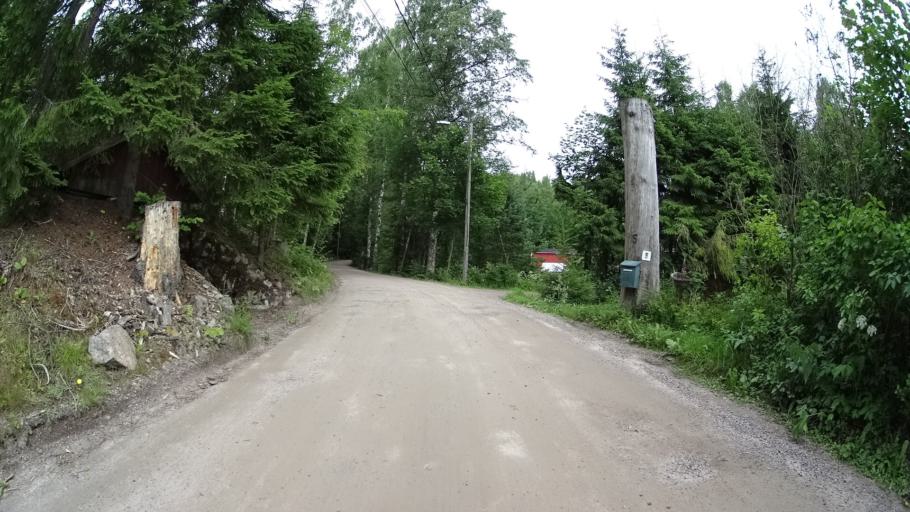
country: FI
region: Uusimaa
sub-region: Helsinki
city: Espoo
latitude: 60.2755
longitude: 24.6573
